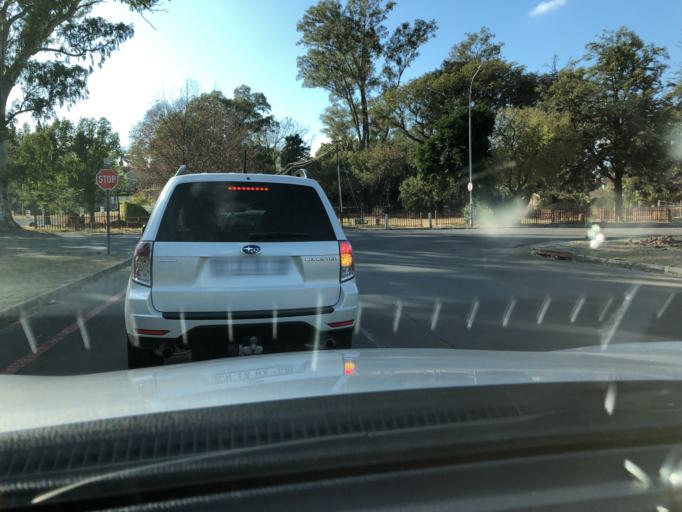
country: ZA
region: KwaZulu-Natal
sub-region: uThukela District Municipality
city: Ladysmith
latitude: -28.5555
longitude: 29.7728
